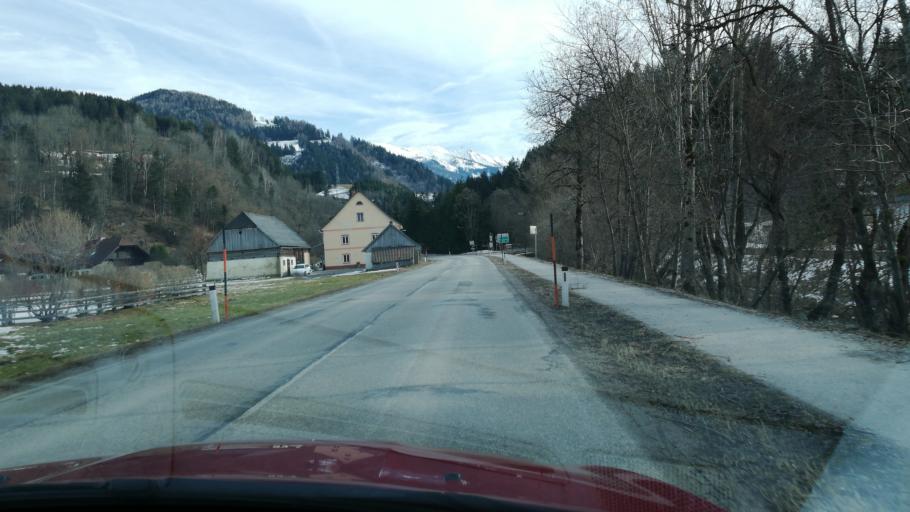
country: AT
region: Styria
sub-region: Politischer Bezirk Liezen
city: Irdning
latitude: 47.4986
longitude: 14.1002
